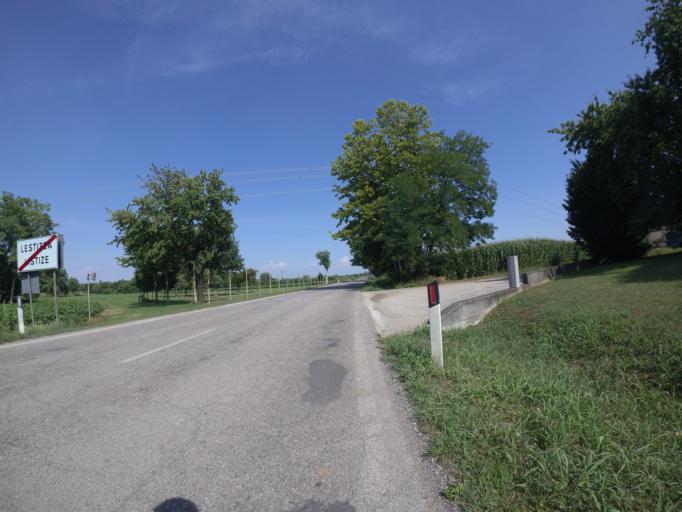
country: IT
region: Friuli Venezia Giulia
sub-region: Provincia di Udine
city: Lestizza
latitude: 45.9558
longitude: 13.1527
